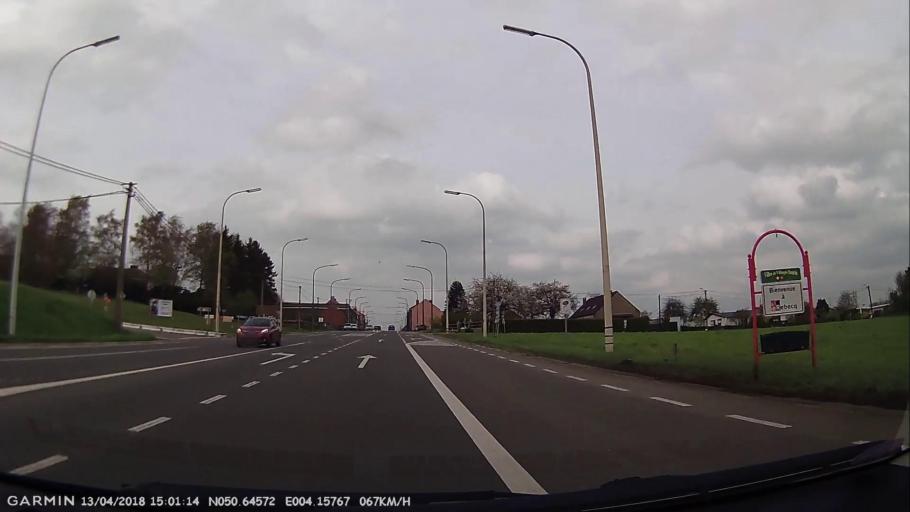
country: BE
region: Wallonia
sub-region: Province du Hainaut
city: Braine-le-Comte
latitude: 50.6458
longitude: 4.1577
